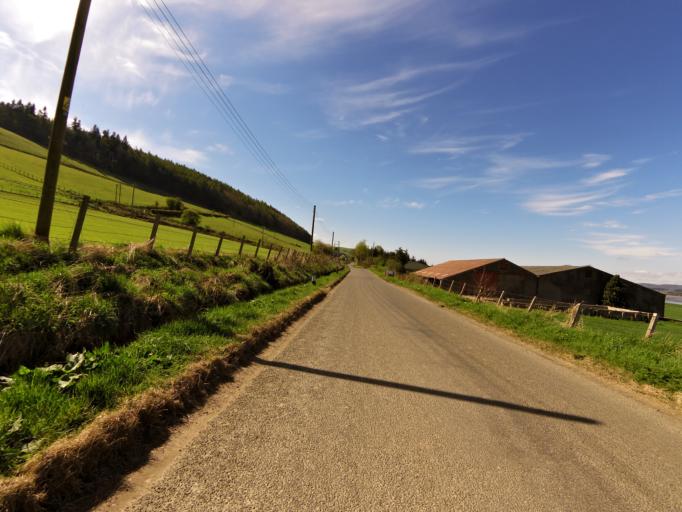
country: GB
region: Scotland
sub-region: Perth and Kinross
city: Errol
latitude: 56.3749
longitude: -3.1511
